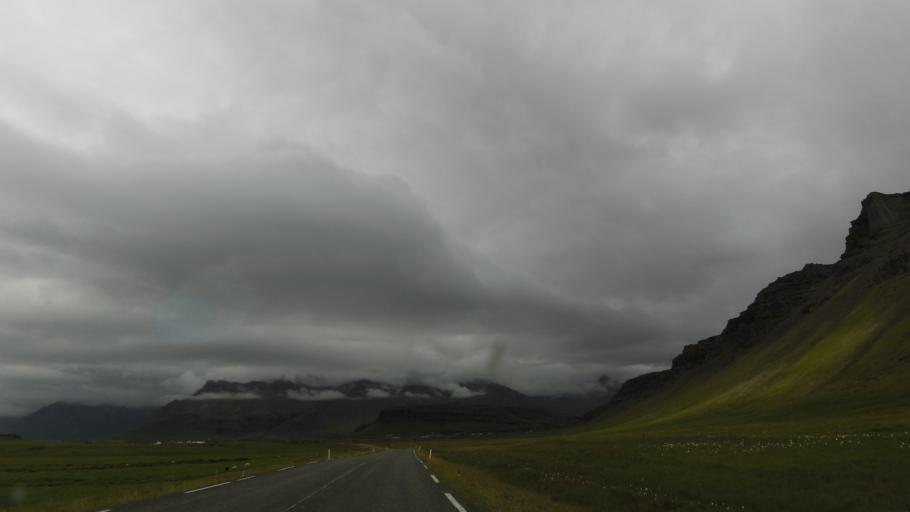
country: IS
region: East
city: Hoefn
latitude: 64.1802
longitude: -15.7815
